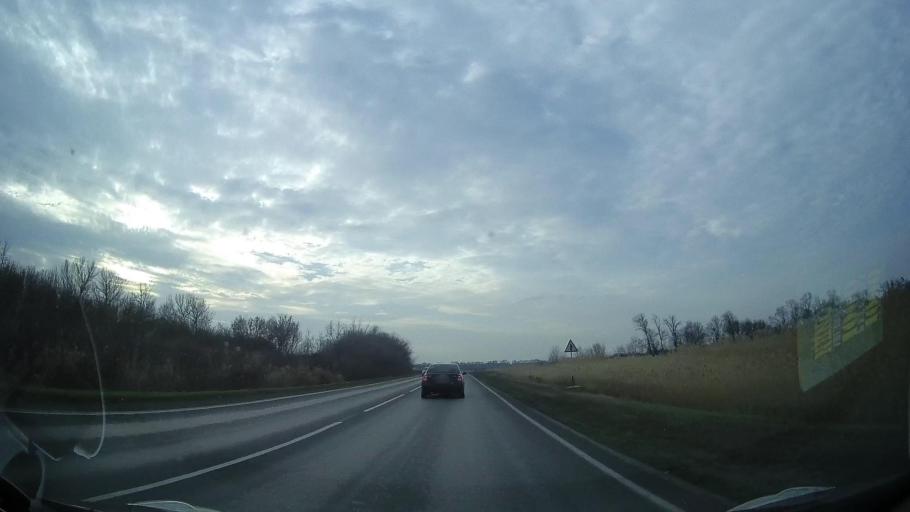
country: RU
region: Rostov
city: Starocherkasskaya
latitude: 47.1392
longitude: 40.0496
